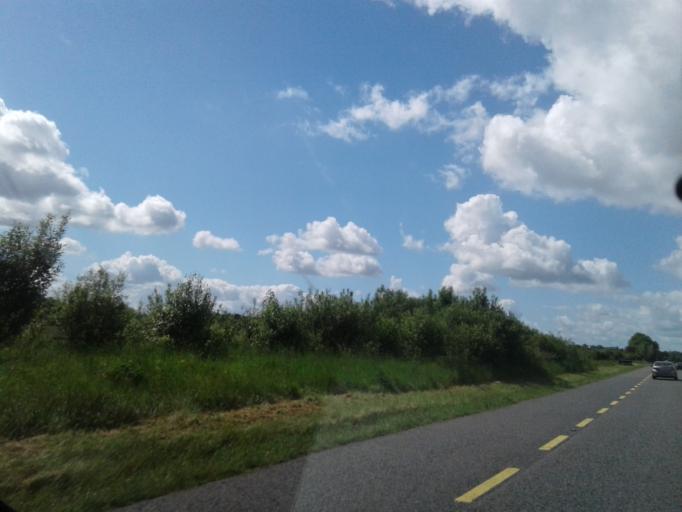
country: IE
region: Leinster
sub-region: An Iarmhi
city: Kilbeggan
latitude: 53.3504
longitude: -7.4988
